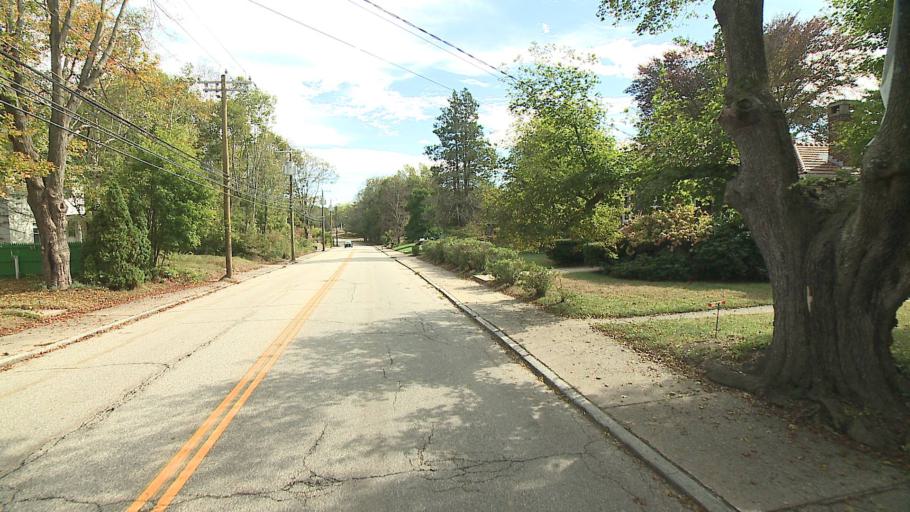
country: US
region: Connecticut
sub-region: Windham County
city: Putnam
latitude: 41.9103
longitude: -71.8997
